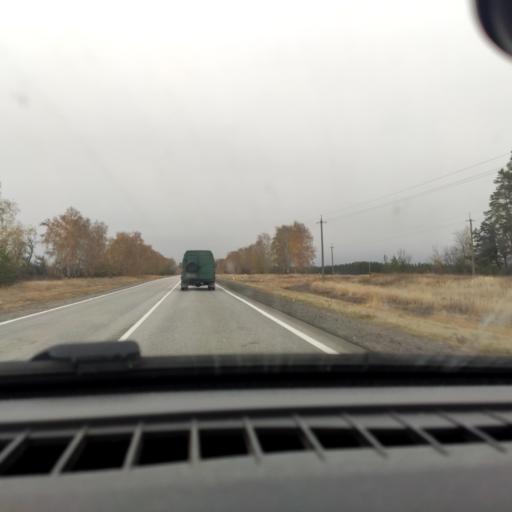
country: RU
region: Voronezj
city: Uryv-Pokrovka
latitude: 51.0597
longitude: 38.9913
